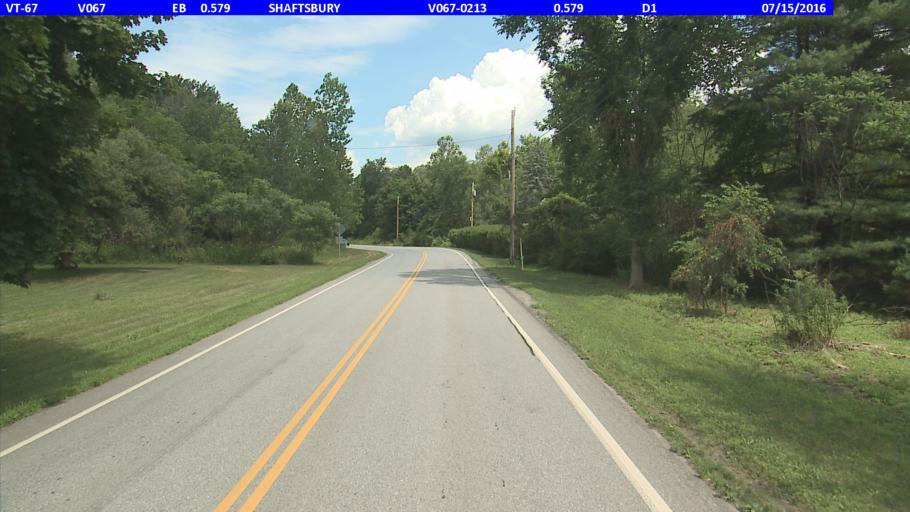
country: US
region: Vermont
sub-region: Bennington County
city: North Bennington
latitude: 42.9363
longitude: -73.2653
